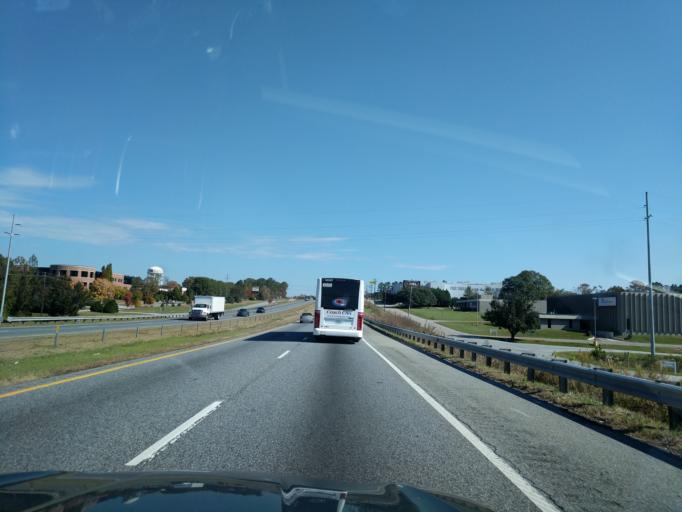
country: US
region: South Carolina
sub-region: Spartanburg County
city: Arcadia
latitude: 34.9713
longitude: -81.9947
